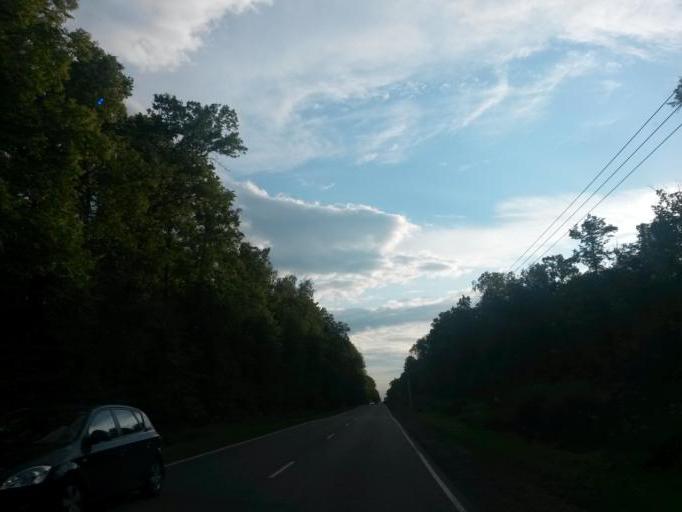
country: RU
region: Moskovskaya
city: Barybino
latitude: 55.1984
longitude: 37.8181
